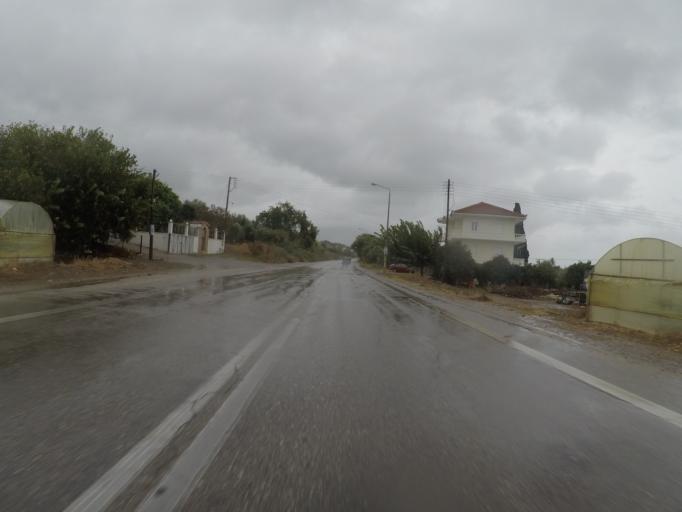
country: GR
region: West Greece
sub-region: Nomos Ileias
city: Zacharo
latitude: 37.4189
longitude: 21.6703
